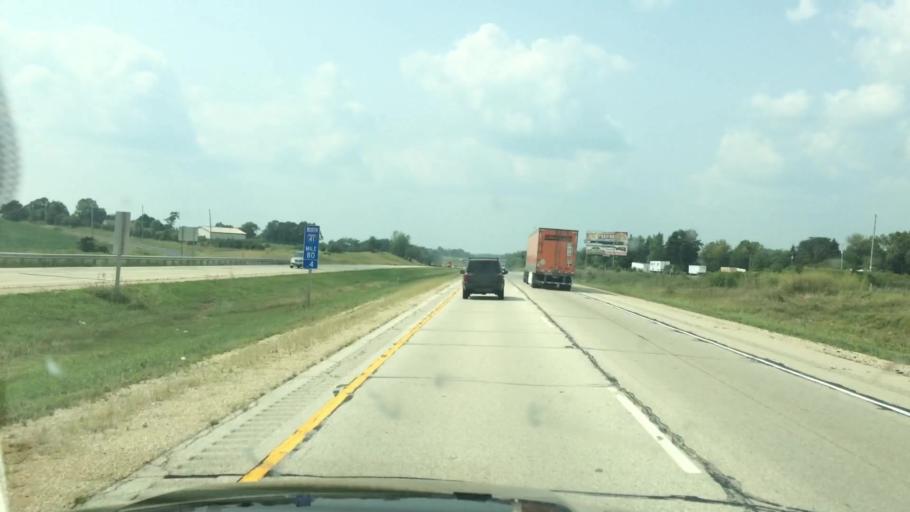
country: US
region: Wisconsin
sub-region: Dodge County
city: Theresa
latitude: 43.5285
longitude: -88.3925
